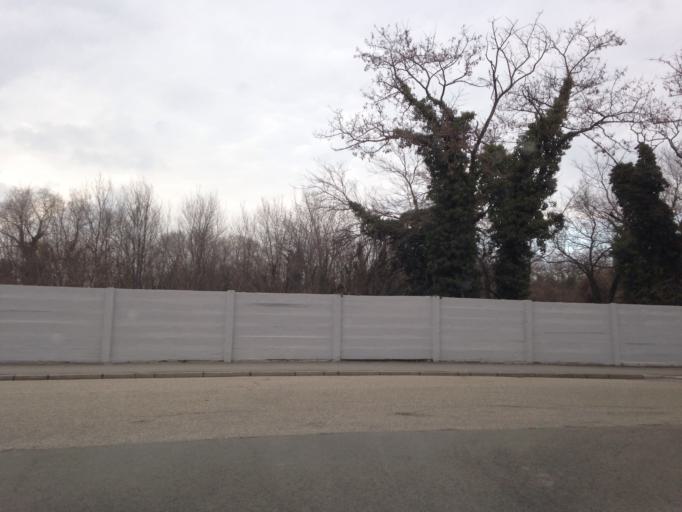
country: SK
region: Nitriansky
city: Komarno
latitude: 47.7639
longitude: 18.1194
